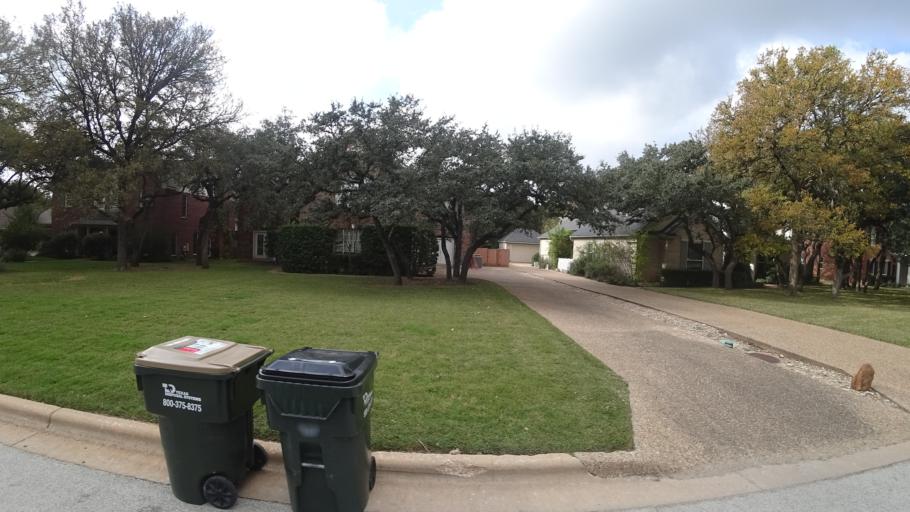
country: US
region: Texas
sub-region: Travis County
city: Barton Creek
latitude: 30.2996
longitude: -97.8949
